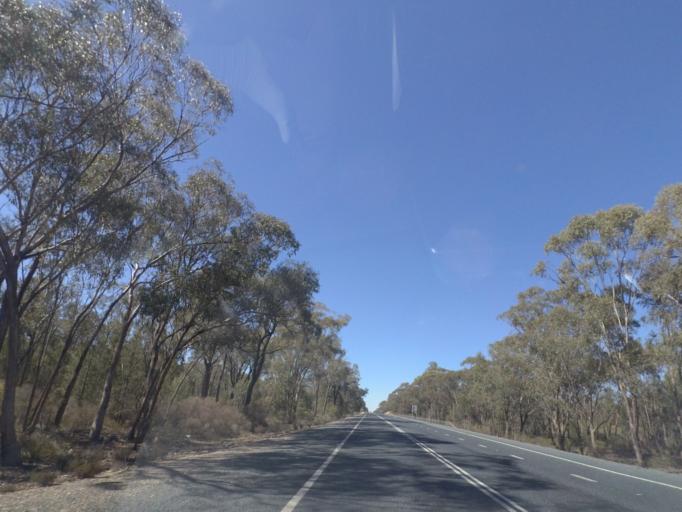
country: AU
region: New South Wales
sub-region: Bland
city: West Wyalong
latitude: -34.1253
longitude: 147.1257
